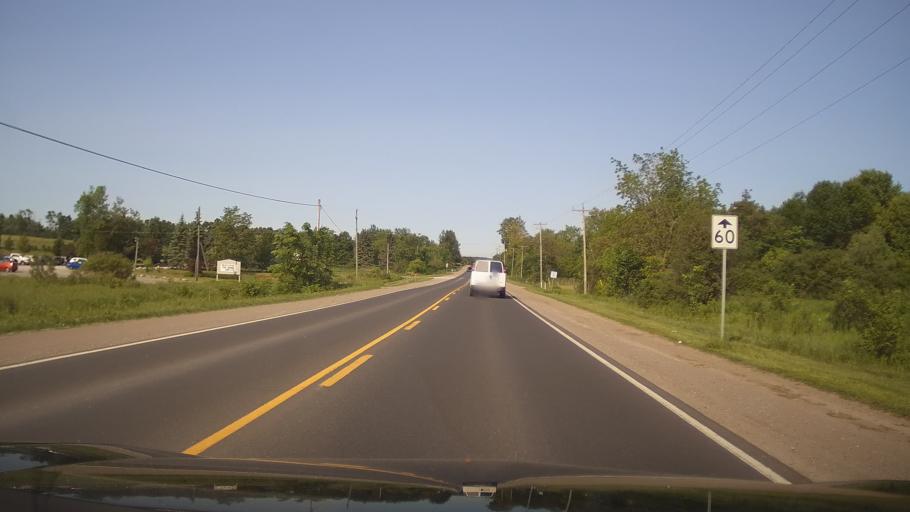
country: CA
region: Ontario
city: Peterborough
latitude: 44.2701
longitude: -78.3954
